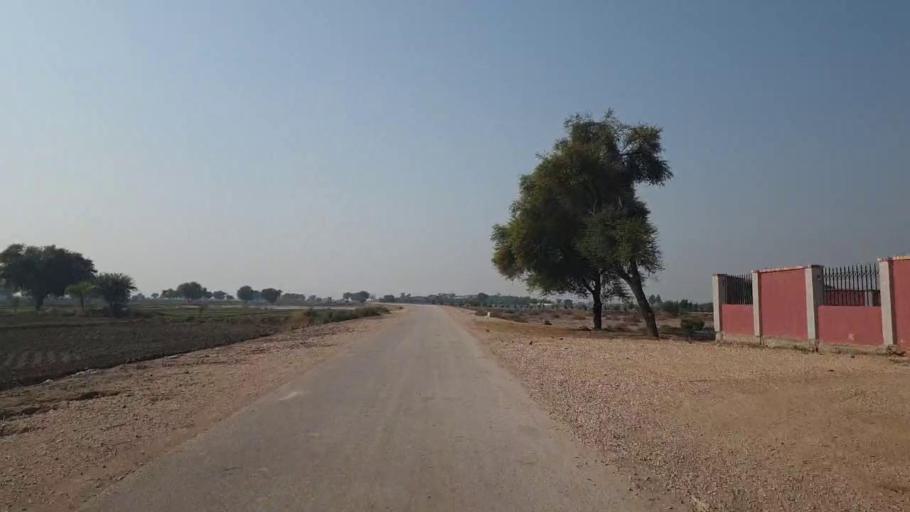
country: PK
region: Sindh
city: Sehwan
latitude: 26.4270
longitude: 67.8350
